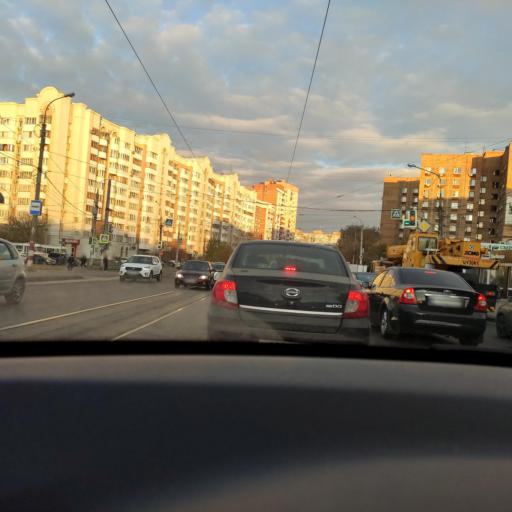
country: RU
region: Samara
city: Samara
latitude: 53.1967
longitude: 50.1577
